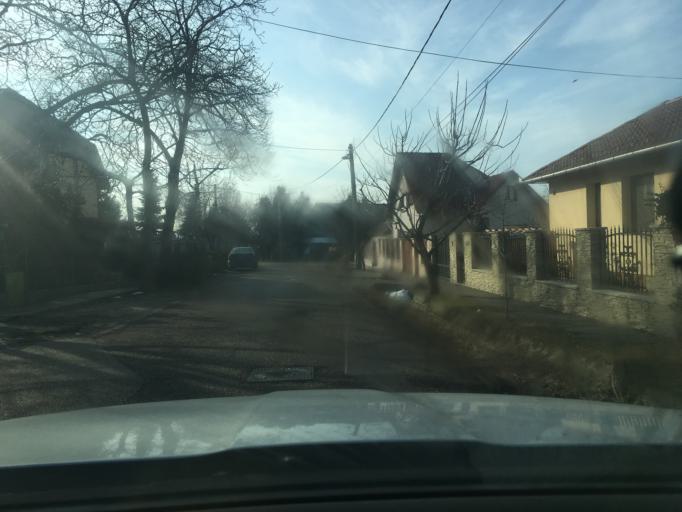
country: HU
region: Budapest
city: Budapest XVI. keruelet
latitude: 47.5015
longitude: 19.1800
